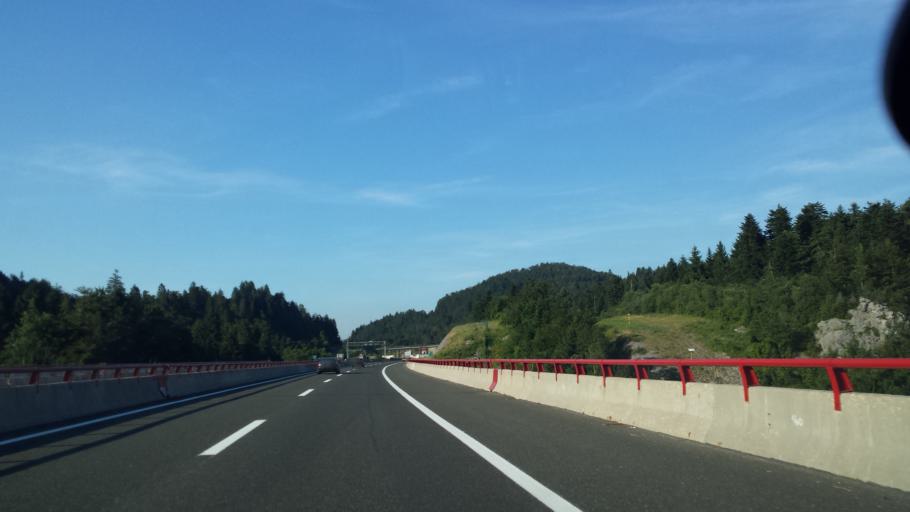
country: HR
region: Primorsko-Goranska
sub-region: Grad Delnice
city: Delnice
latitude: 45.3582
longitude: 14.7631
